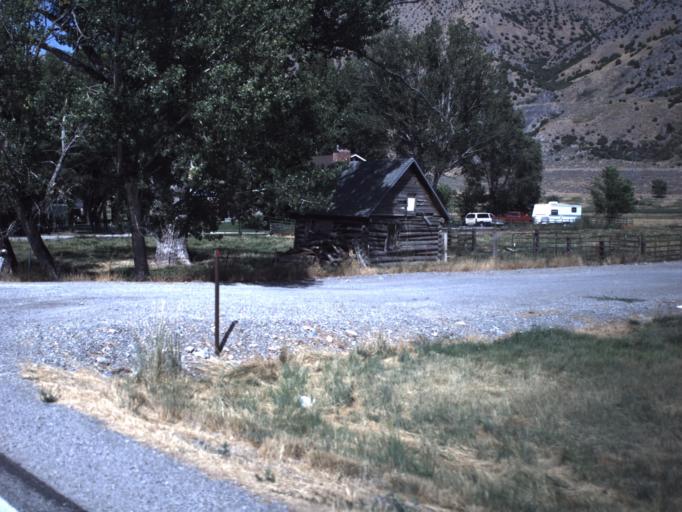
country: US
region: Utah
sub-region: Box Elder County
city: Elwood
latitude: 41.6940
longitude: -112.0900
